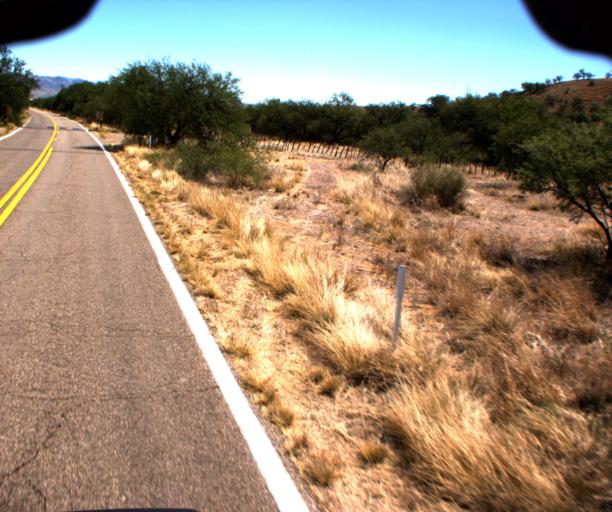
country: US
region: Arizona
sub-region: Santa Cruz County
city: Rio Rico
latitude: 31.4234
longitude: -111.0111
